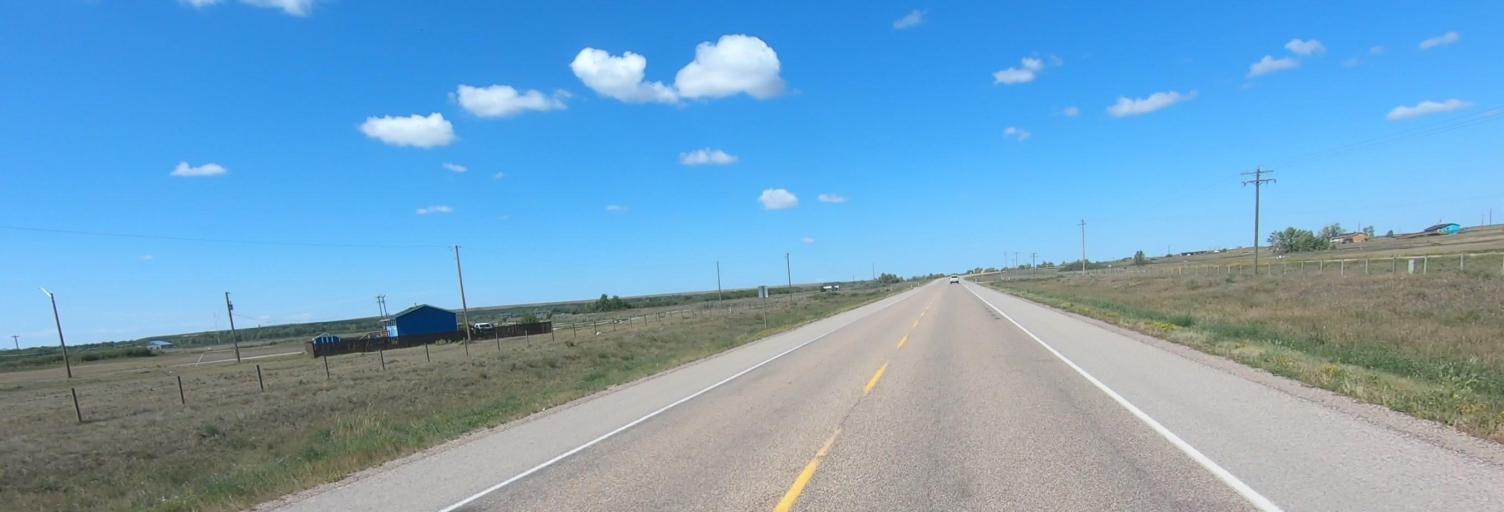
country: CA
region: Alberta
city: Strathmore
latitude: 50.8540
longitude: -113.1240
